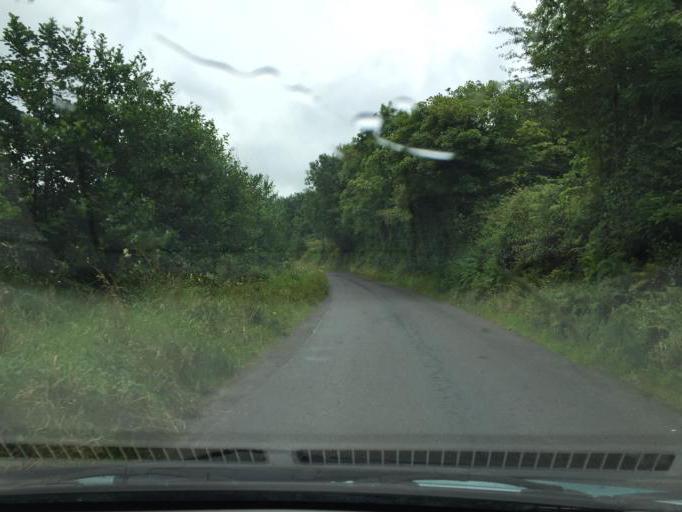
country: IE
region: Connaught
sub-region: Sligo
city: Sligo
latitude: 54.2358
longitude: -8.4522
